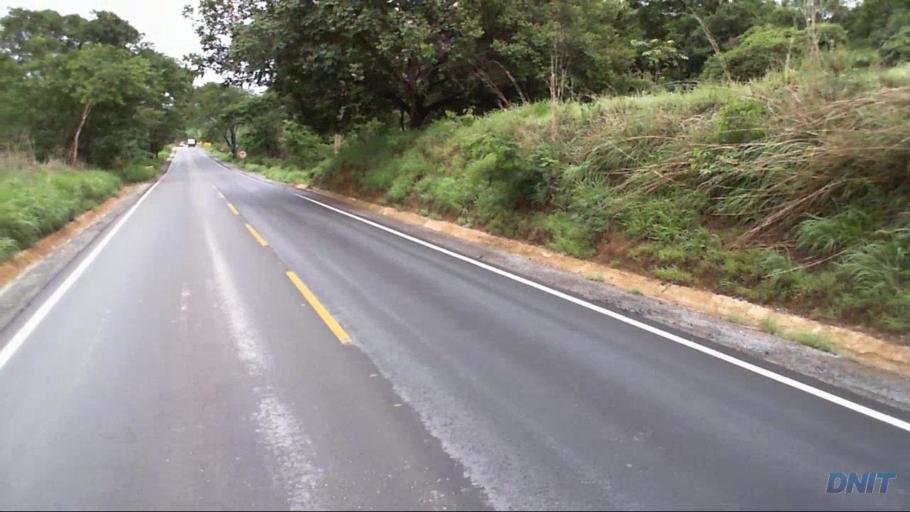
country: BR
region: Goias
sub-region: Padre Bernardo
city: Padre Bernardo
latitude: -15.5021
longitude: -48.2139
